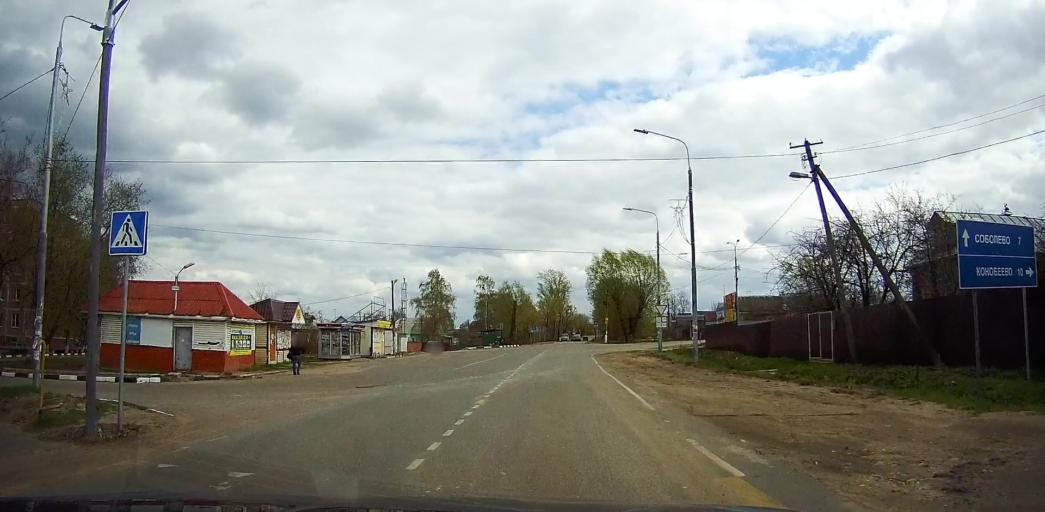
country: RU
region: Moskovskaya
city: Imeni Tsyurupy
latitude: 55.4976
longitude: 38.6454
